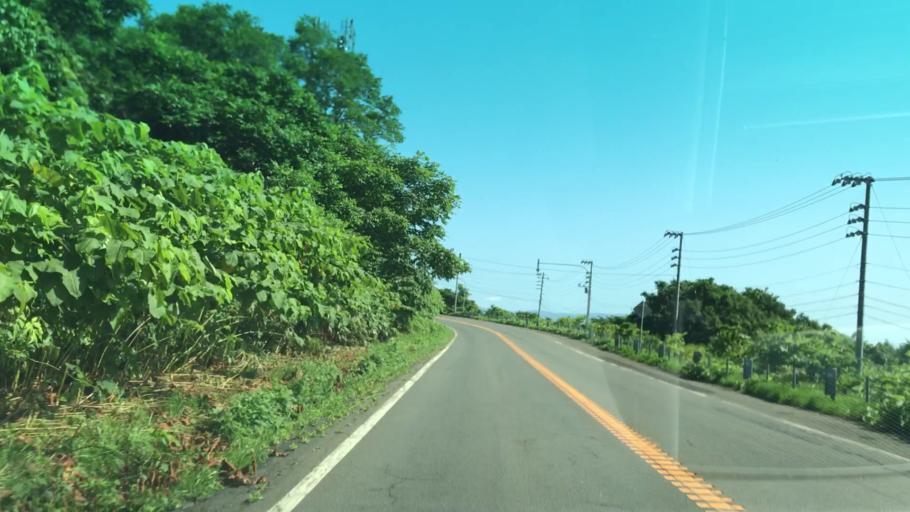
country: JP
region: Hokkaido
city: Iwanai
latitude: 43.1368
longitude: 140.4298
